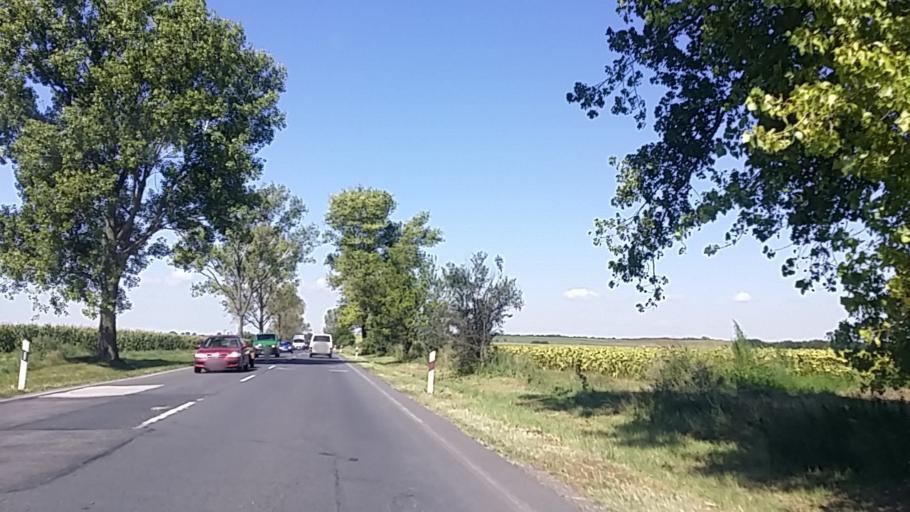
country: HU
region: Tolna
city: Simontornya
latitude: 46.7652
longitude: 18.5898
